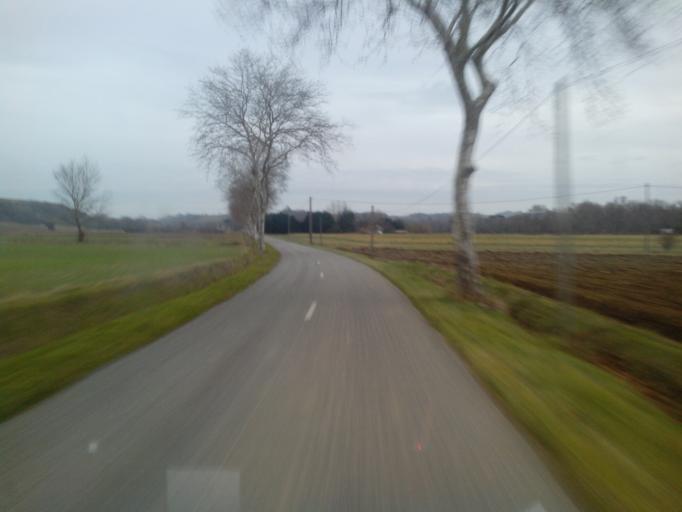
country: FR
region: Midi-Pyrenees
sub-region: Departement de l'Ariege
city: Mazeres
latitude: 43.2481
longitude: 1.7015
